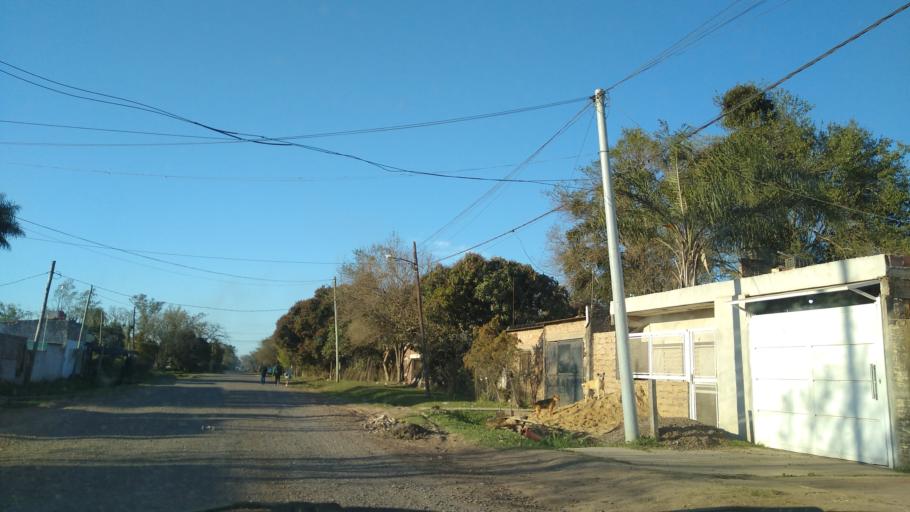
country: AR
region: Chaco
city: Barranqueras
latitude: -27.4677
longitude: -58.9496
